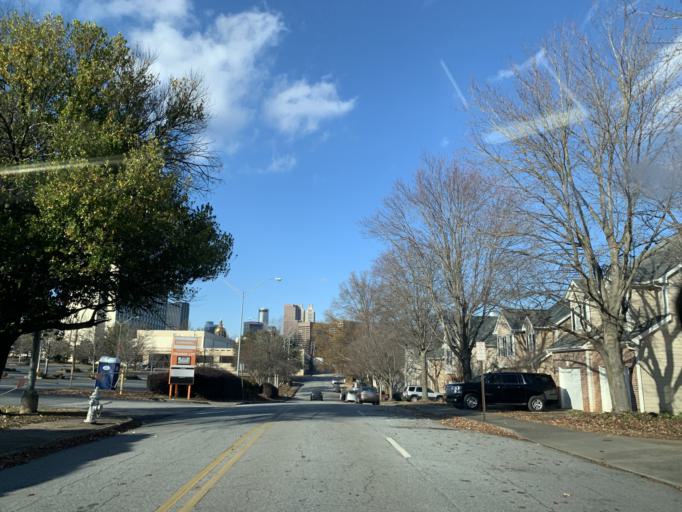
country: US
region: Georgia
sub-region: Fulton County
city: Atlanta
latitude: 33.7403
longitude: -84.3863
